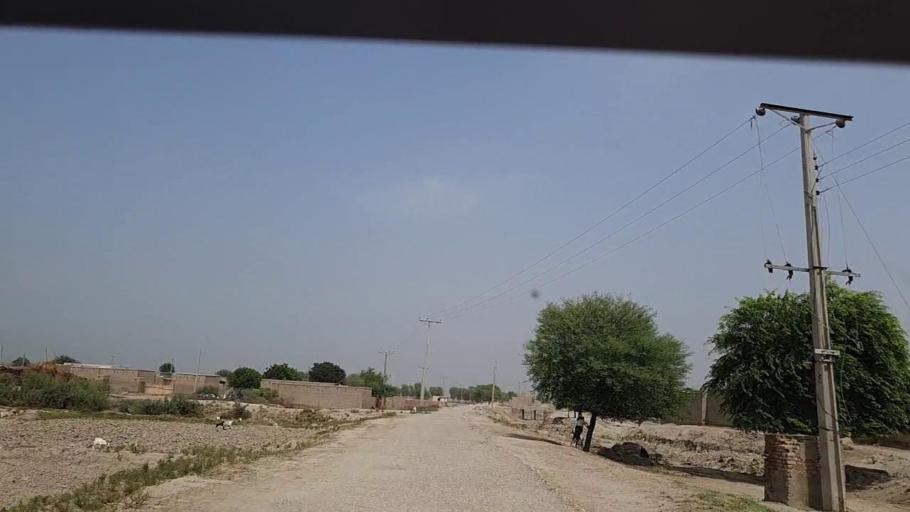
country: PK
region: Sindh
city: Khairpur Nathan Shah
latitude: 27.0810
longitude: 67.6749
